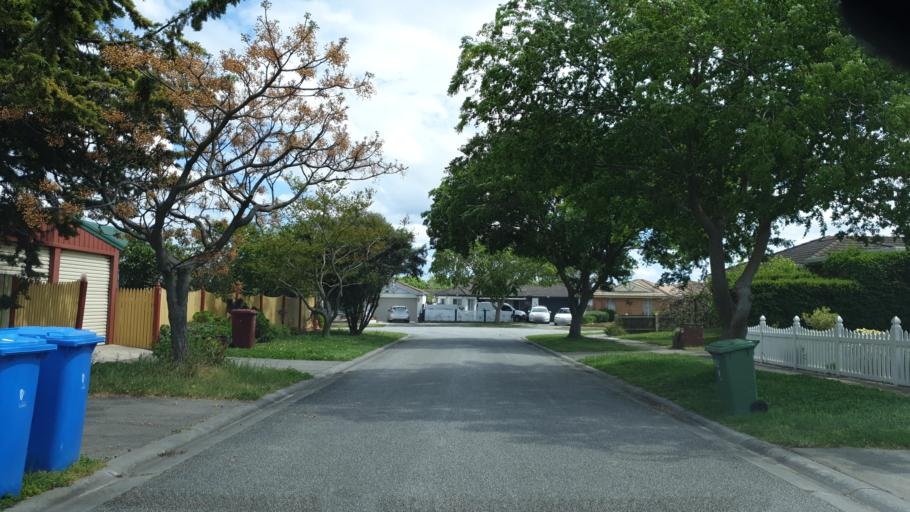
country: AU
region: Victoria
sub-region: Casey
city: Cranbourne North
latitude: -38.0770
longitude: 145.2936
